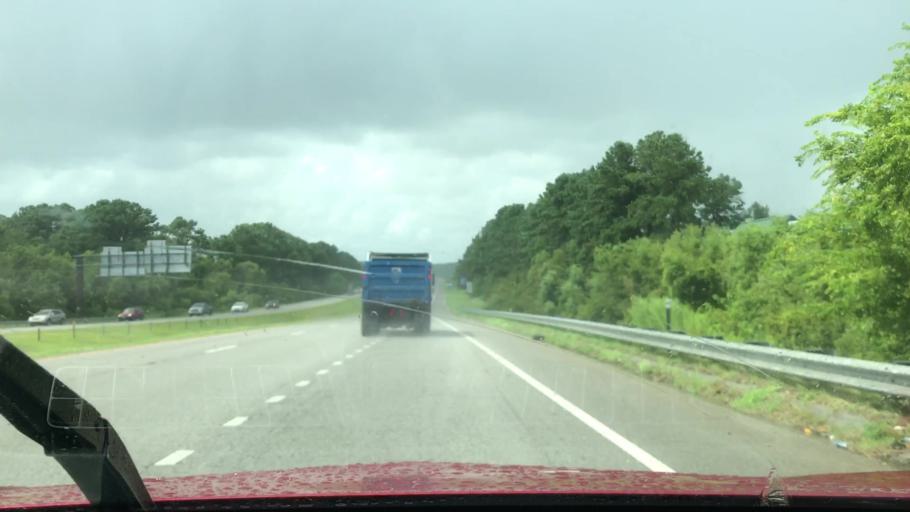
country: US
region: South Carolina
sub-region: Charleston County
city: Mount Pleasant
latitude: 32.8249
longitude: -79.8500
